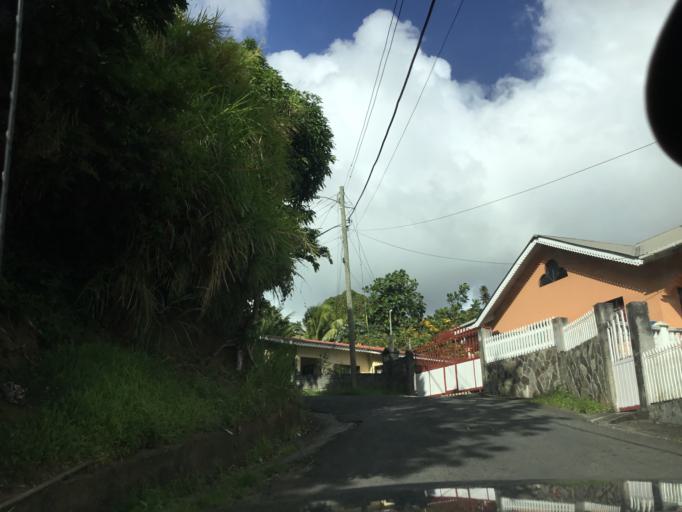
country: VC
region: Saint George
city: Kingstown
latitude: 13.1697
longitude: -61.2200
